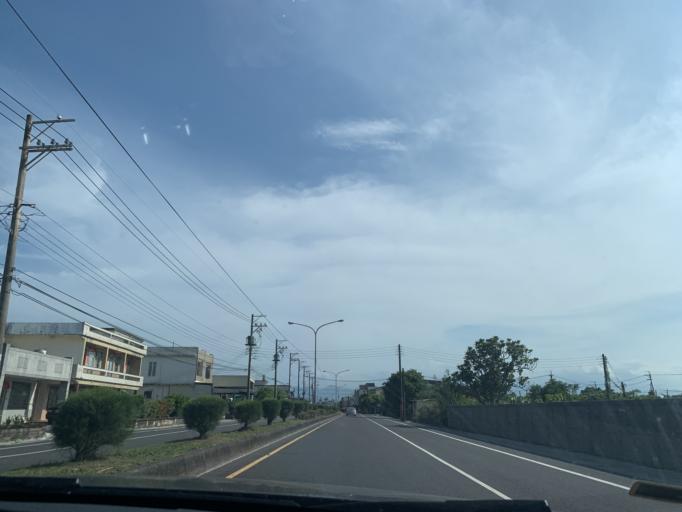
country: TW
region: Taiwan
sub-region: Yilan
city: Yilan
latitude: 24.8297
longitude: 121.8220
